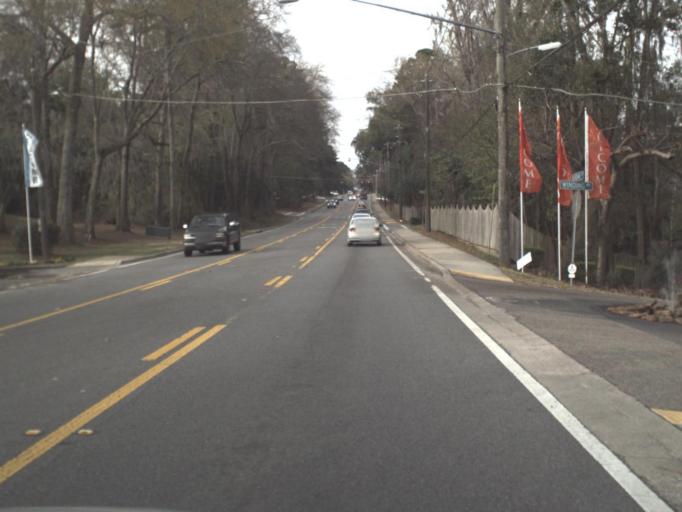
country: US
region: Florida
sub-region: Leon County
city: Tallahassee
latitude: 30.4699
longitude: -84.2772
